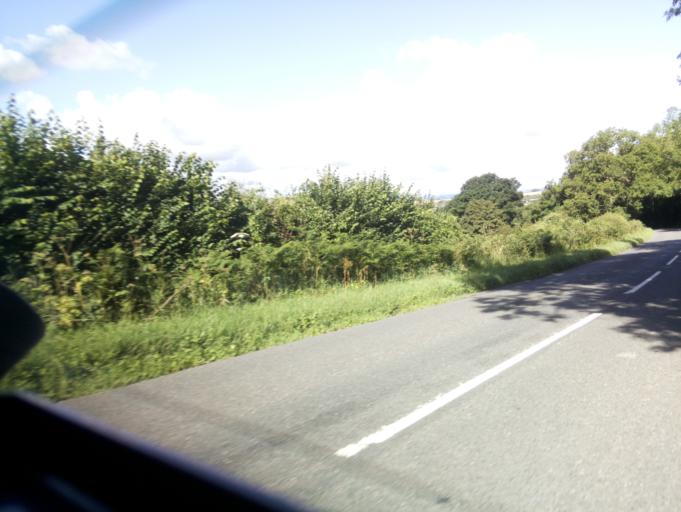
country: GB
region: England
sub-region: Herefordshire
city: Linton
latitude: 51.9379
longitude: -2.5142
